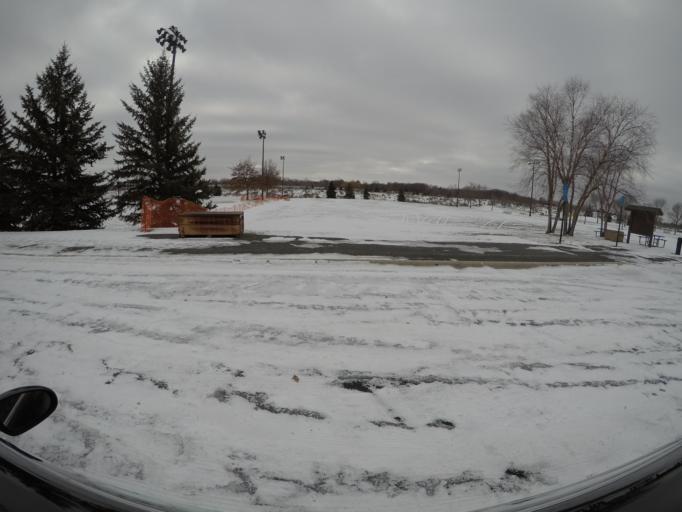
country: US
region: Minnesota
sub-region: Hennepin County
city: Eden Prairie
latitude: 44.8519
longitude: -93.4958
